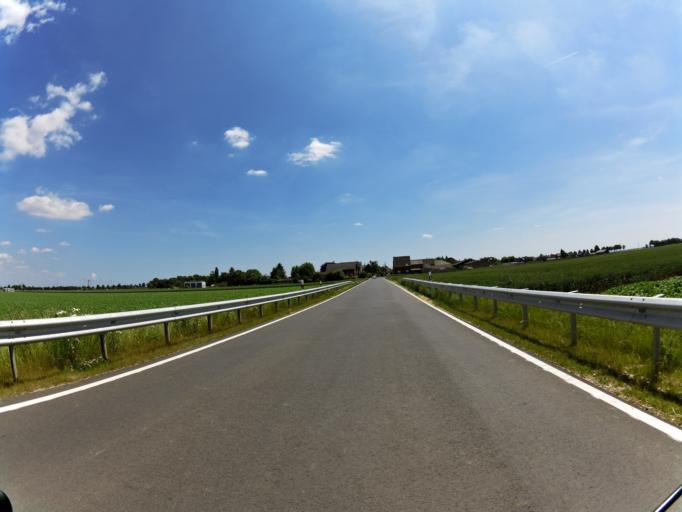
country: DE
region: North Rhine-Westphalia
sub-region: Regierungsbezirk Koln
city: Heinsberg
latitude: 51.0201
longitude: 6.0685
